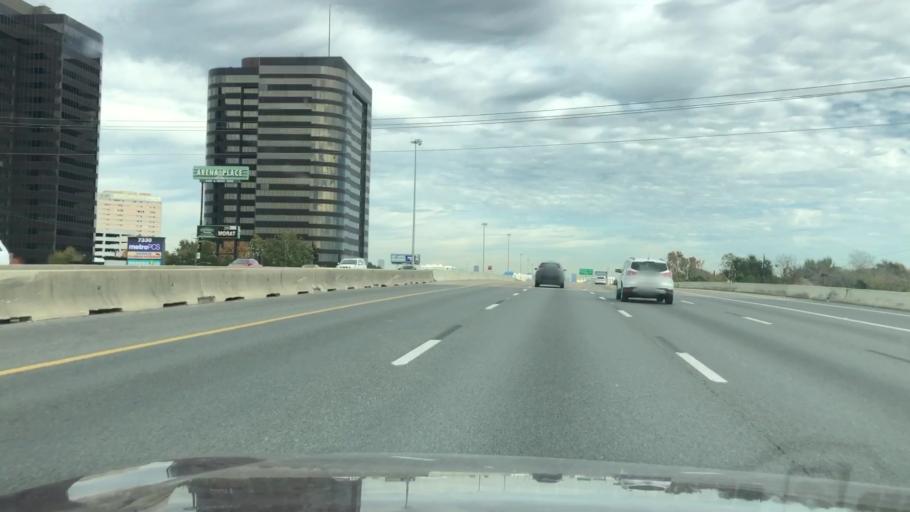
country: US
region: Texas
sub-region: Harris County
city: Bellaire
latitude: 29.6997
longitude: -95.5183
